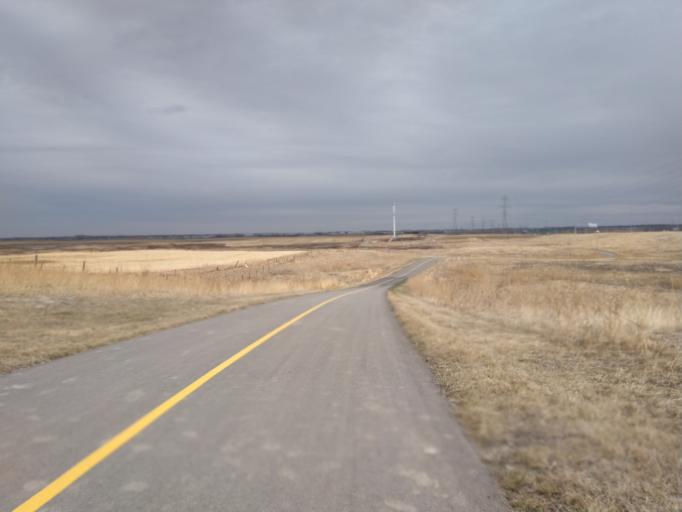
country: CA
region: Alberta
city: Airdrie
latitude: 51.1756
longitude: -114.0558
